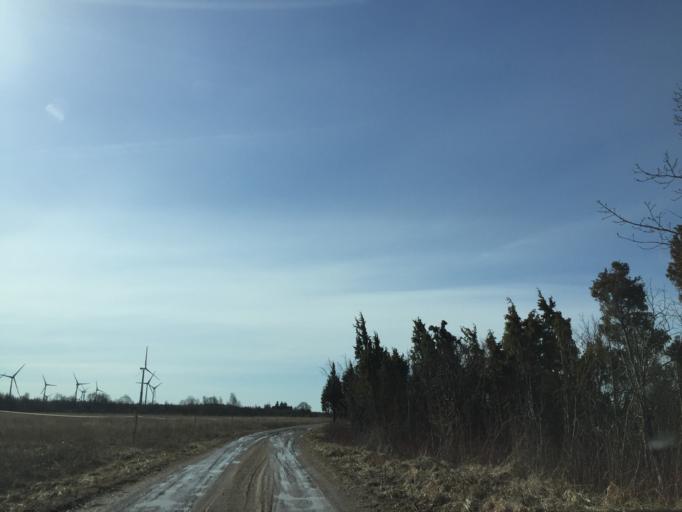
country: EE
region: Laeaene
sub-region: Haapsalu linn
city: Haapsalu
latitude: 58.6517
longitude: 23.5136
